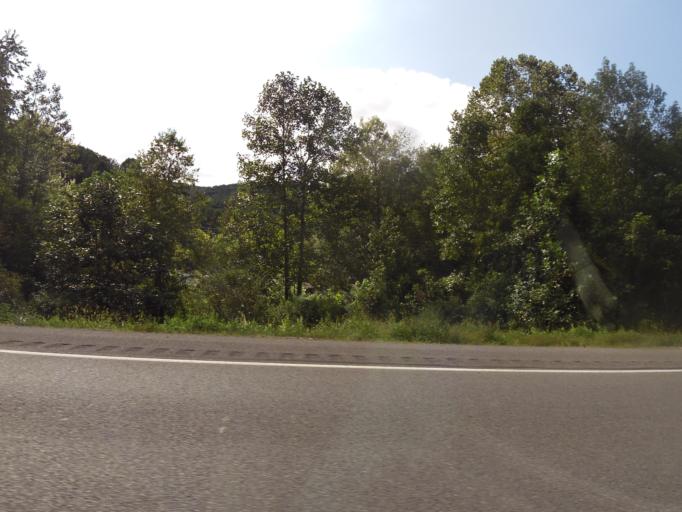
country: US
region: Kentucky
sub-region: Bell County
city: Pineville
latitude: 36.7062
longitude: -83.6968
